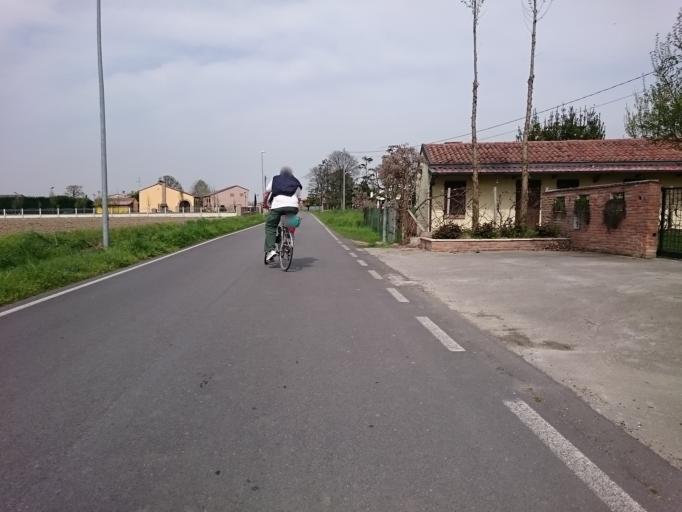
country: IT
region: Veneto
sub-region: Provincia di Padova
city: Tribano
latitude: 45.1955
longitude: 11.8269
